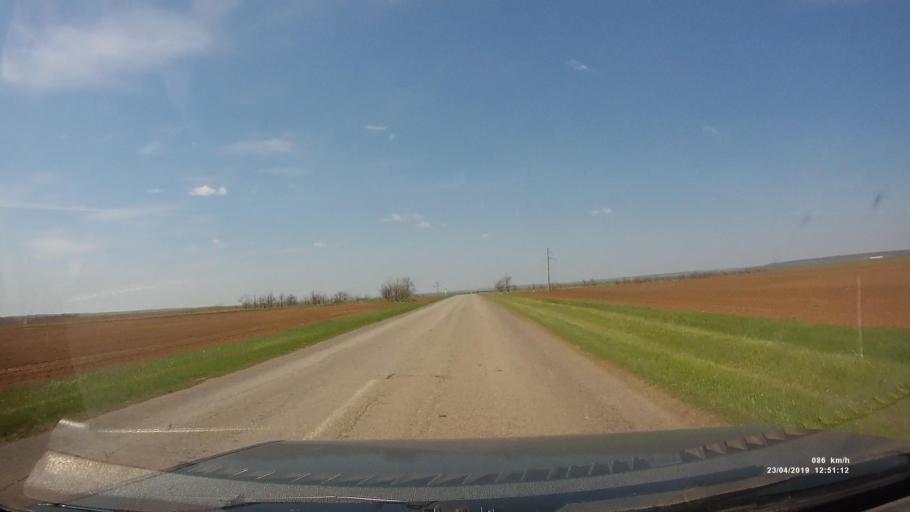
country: RU
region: Kalmykiya
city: Yashalta
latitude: 46.5526
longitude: 42.6259
